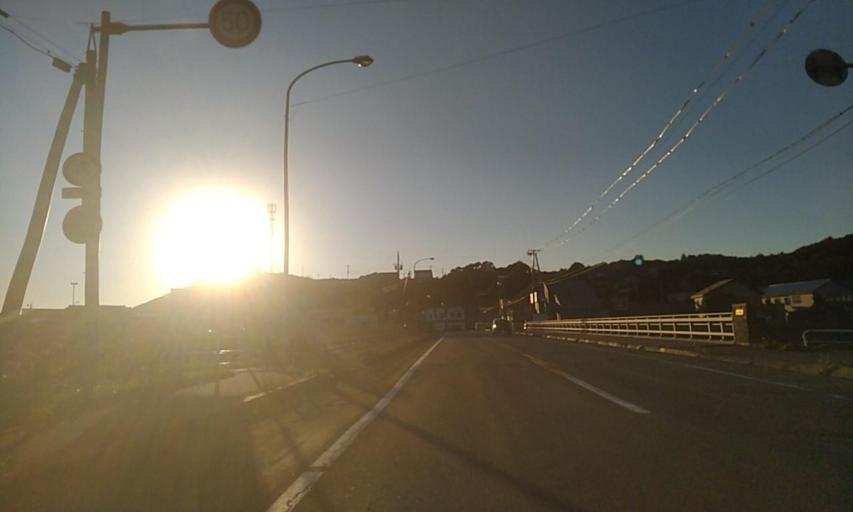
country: JP
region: Hokkaido
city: Shizunai-furukawacho
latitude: 42.1278
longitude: 142.9299
